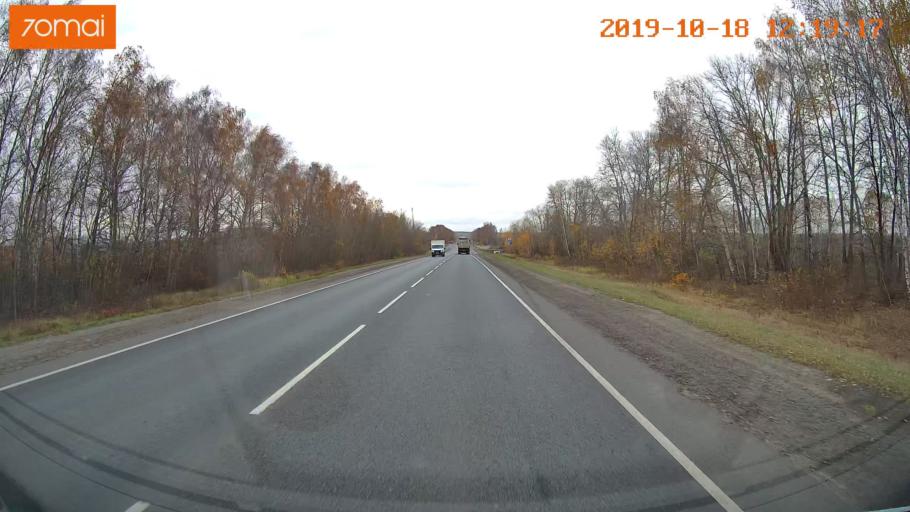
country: RU
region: Rjazan
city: Zakharovo
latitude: 54.4801
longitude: 39.4664
